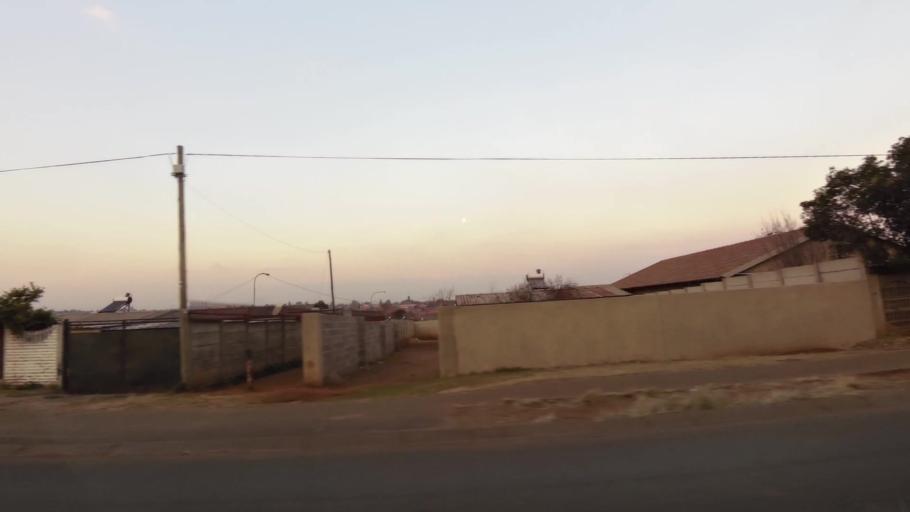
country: ZA
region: Gauteng
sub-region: City of Johannesburg Metropolitan Municipality
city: Soweto
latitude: -26.2906
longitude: 27.8807
